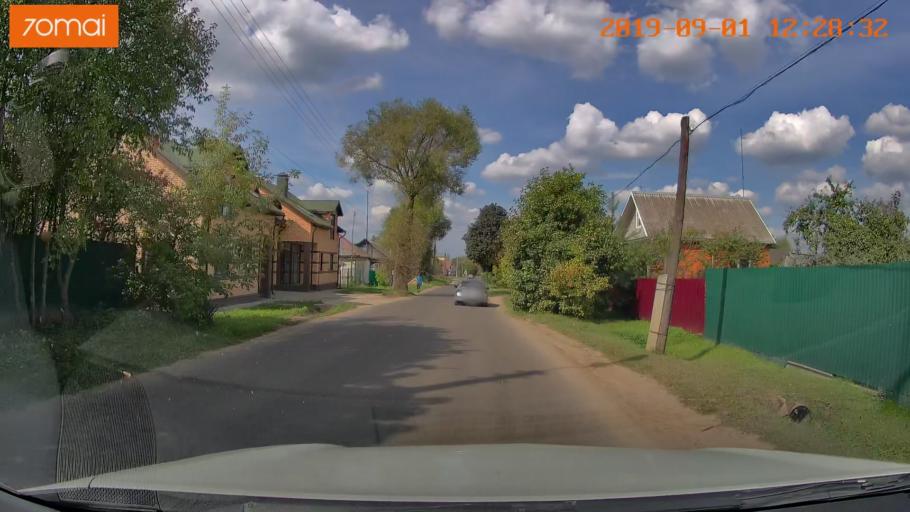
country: RU
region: Kaluga
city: Maloyaroslavets
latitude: 55.0066
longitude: 36.4526
